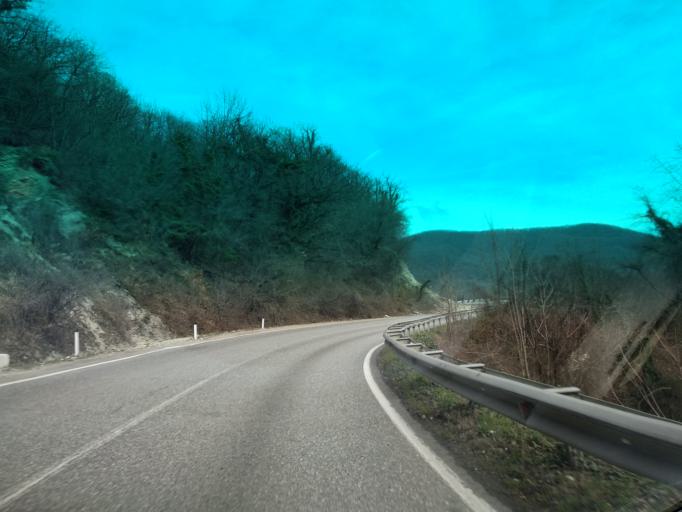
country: RU
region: Krasnodarskiy
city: Shepsi
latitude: 44.0688
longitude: 39.1383
